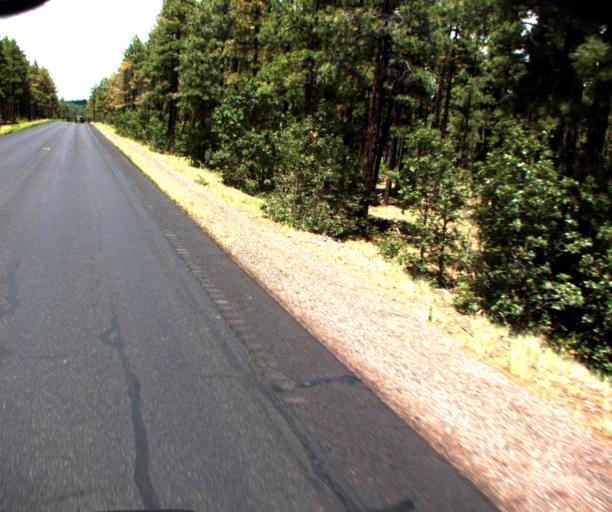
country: US
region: Arizona
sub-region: Gila County
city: Pine
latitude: 34.4883
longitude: -111.4562
